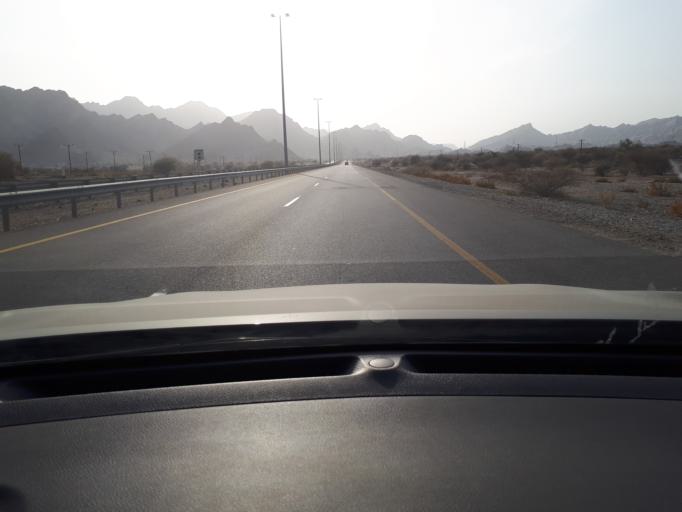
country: OM
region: Muhafazat Masqat
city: Muscat
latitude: 23.3645
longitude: 58.6585
